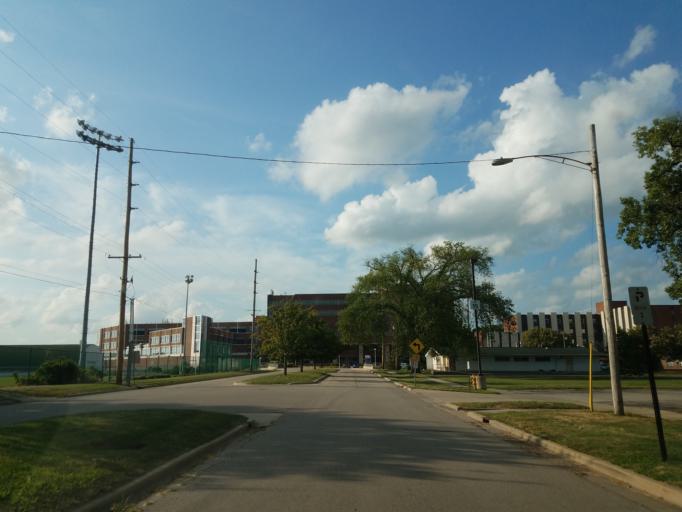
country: US
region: Illinois
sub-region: McLean County
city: Bloomington
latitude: 40.4951
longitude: -88.9908
